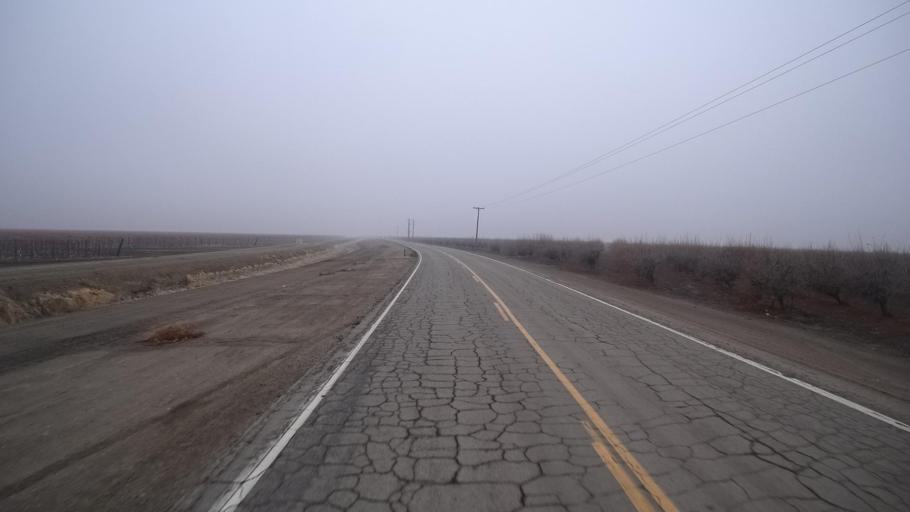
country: US
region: California
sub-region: Kern County
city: Lost Hills
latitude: 35.5127
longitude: -119.6146
